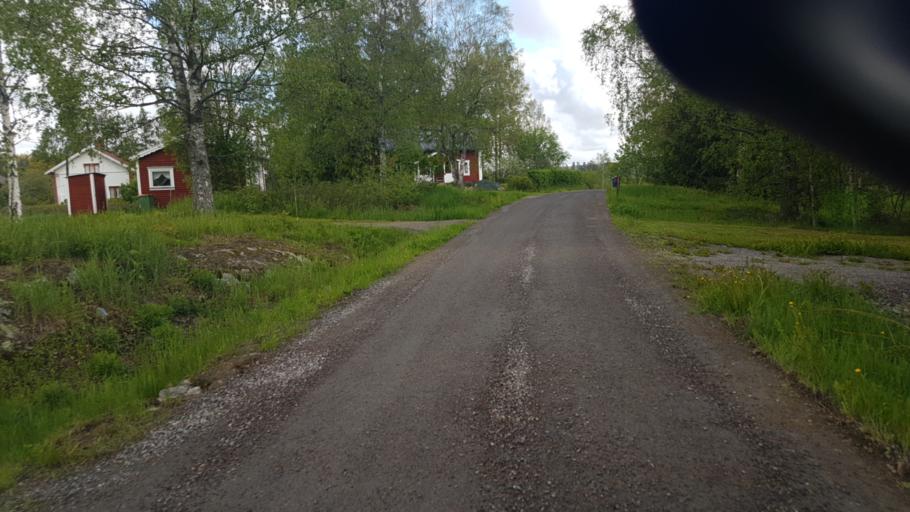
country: NO
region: Ostfold
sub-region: Romskog
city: Romskog
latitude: 59.8615
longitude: 11.9692
